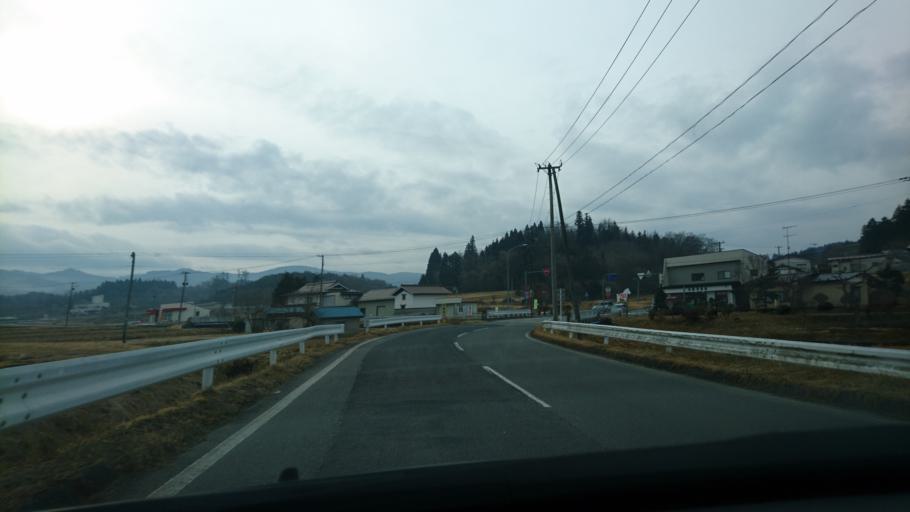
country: JP
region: Iwate
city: Ichinoseki
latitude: 38.9030
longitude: 141.3767
